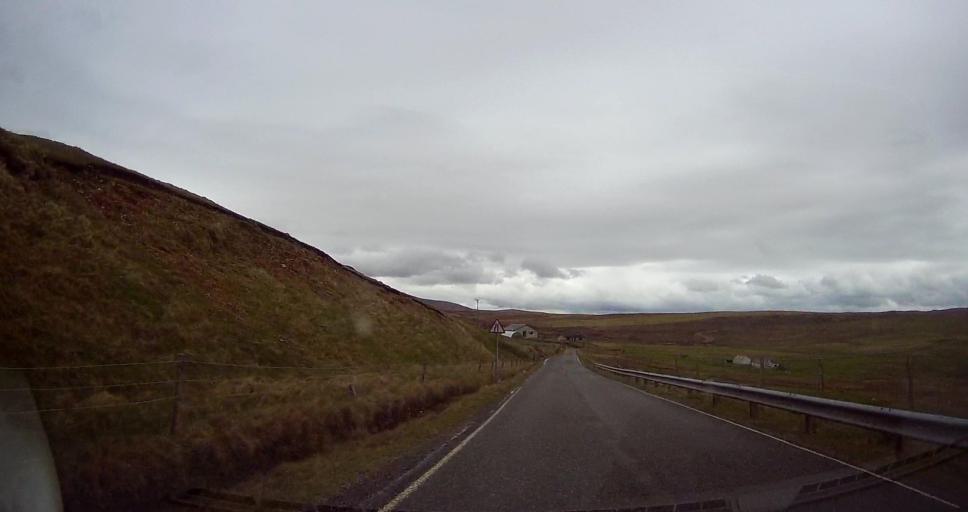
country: GB
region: Scotland
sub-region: Shetland Islands
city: Lerwick
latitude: 60.4868
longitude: -1.4979
